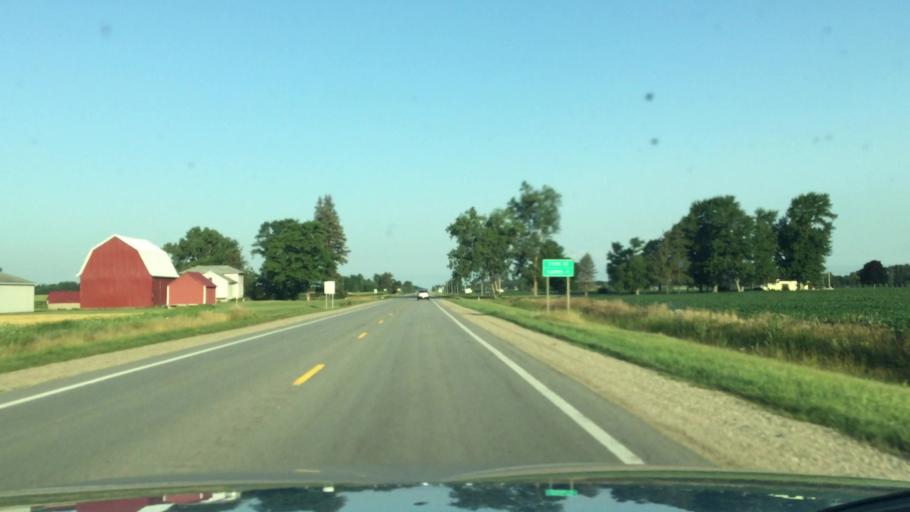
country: US
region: Michigan
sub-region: Gratiot County
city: Ithaca
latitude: 43.1759
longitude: -84.5973
